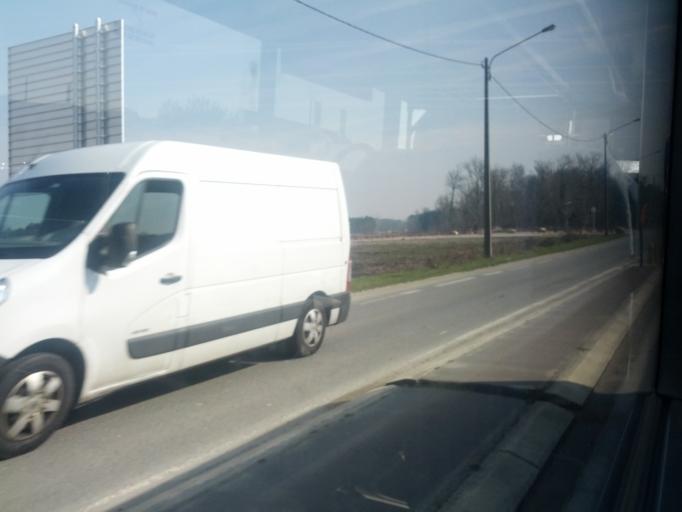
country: FR
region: Aquitaine
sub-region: Departement de la Gironde
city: Le Haillan
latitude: 44.8481
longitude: -0.7053
